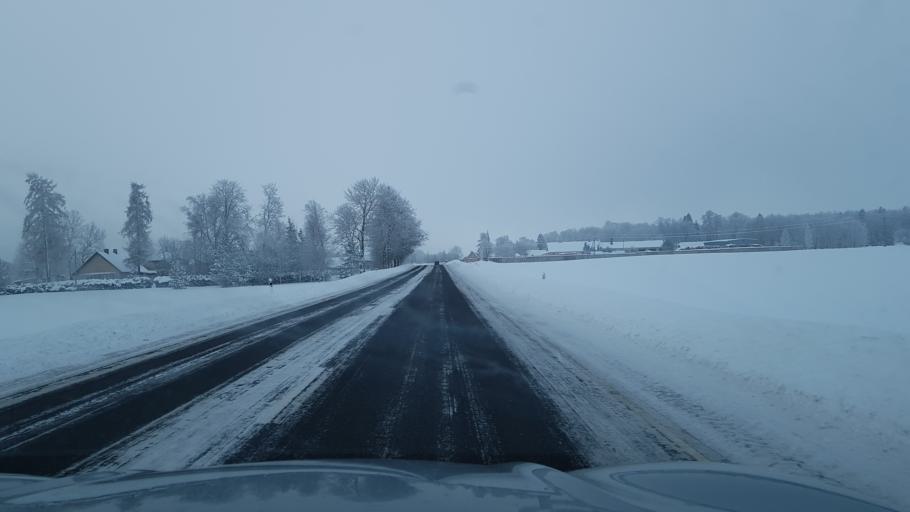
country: EE
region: Ida-Virumaa
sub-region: Johvi vald
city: Johvi
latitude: 59.2644
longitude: 27.3844
